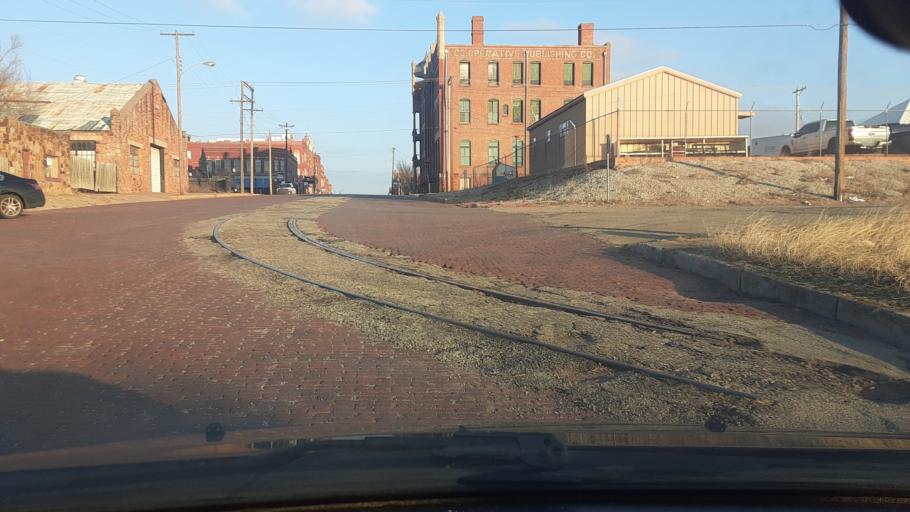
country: US
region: Oklahoma
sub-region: Logan County
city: Guthrie
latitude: 35.8769
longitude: -97.4290
